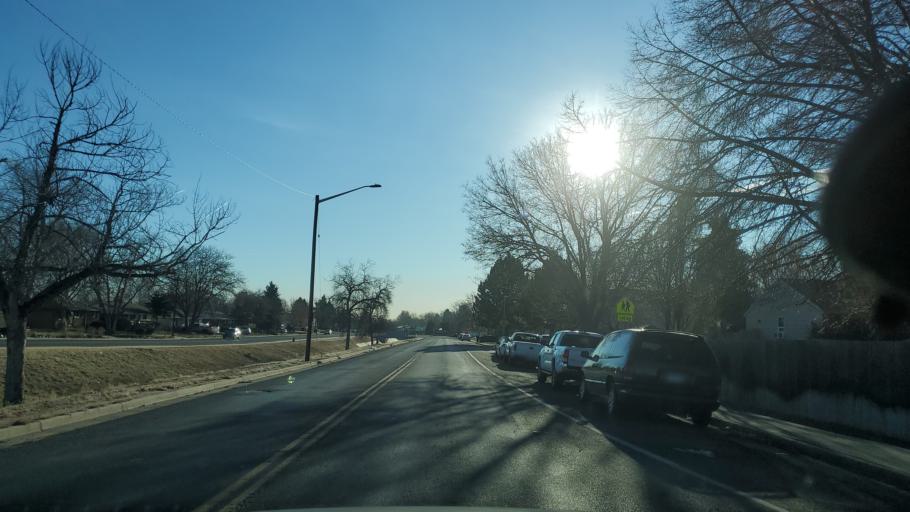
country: US
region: Colorado
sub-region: Adams County
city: Welby
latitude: 39.8463
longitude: -104.9755
